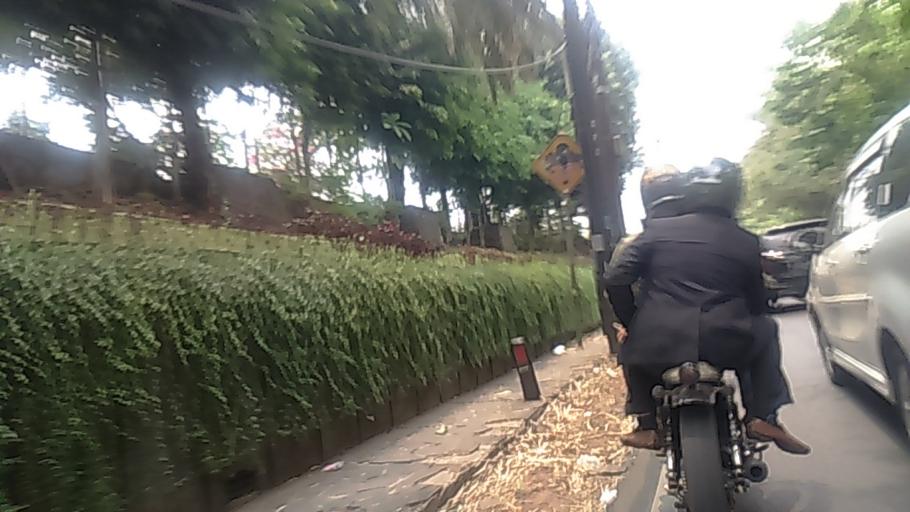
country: ID
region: West Java
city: Pamulang
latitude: -6.3008
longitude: 106.7742
